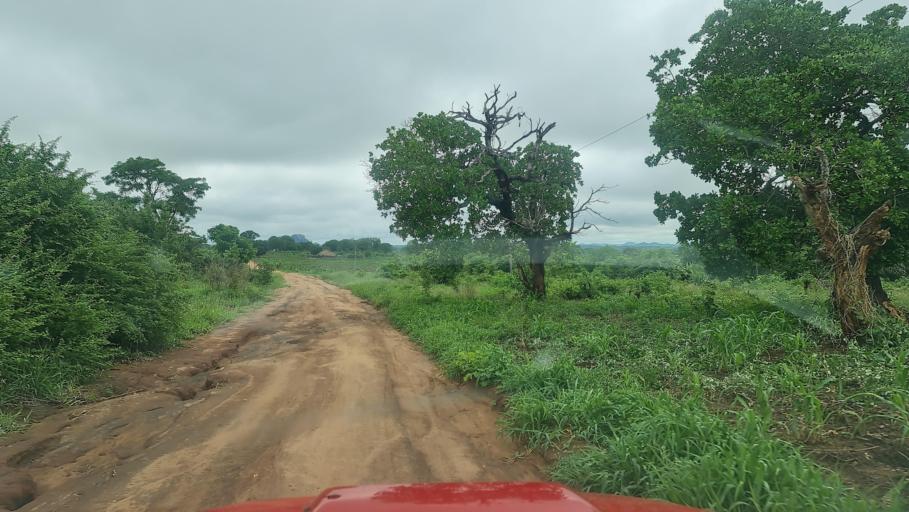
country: MW
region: Southern Region
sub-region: Nsanje District
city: Nsanje
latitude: -17.1982
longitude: 35.8418
